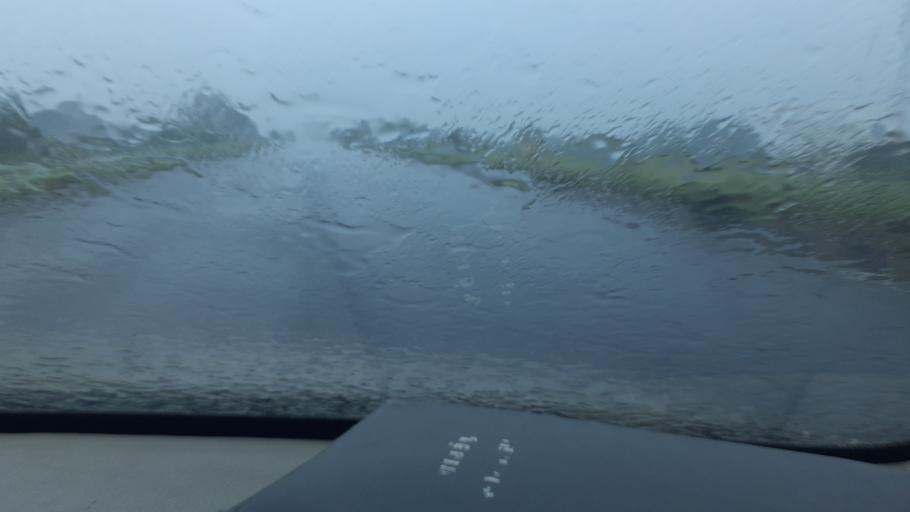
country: IN
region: Tamil Nadu
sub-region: Virudhunagar
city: Sattur
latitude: 9.4451
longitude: 77.9265
